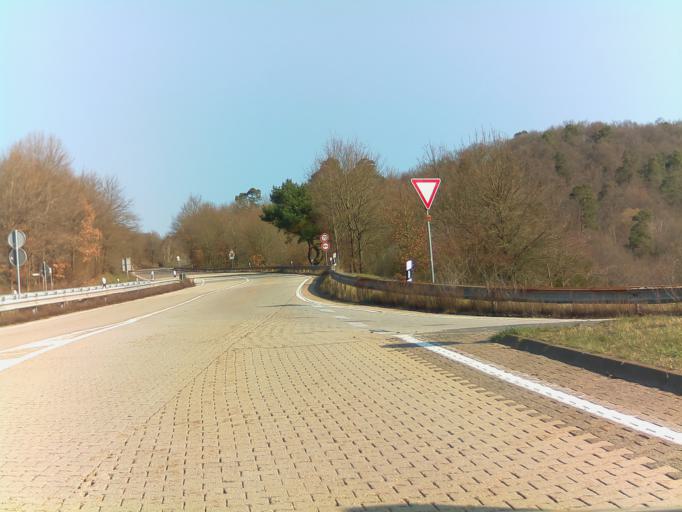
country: DE
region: Rheinland-Pfalz
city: Idar-Oberstein
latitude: 49.7014
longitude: 7.2982
